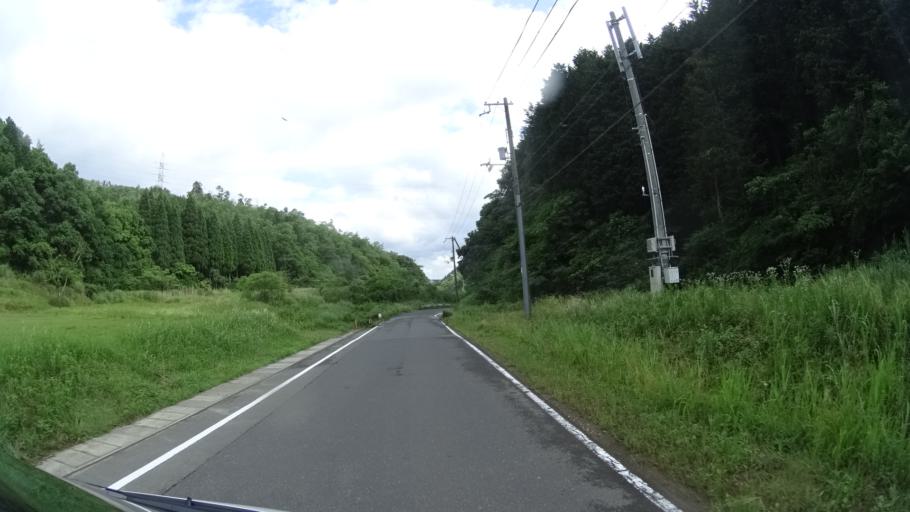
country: JP
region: Kyoto
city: Ayabe
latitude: 35.3676
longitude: 135.2886
